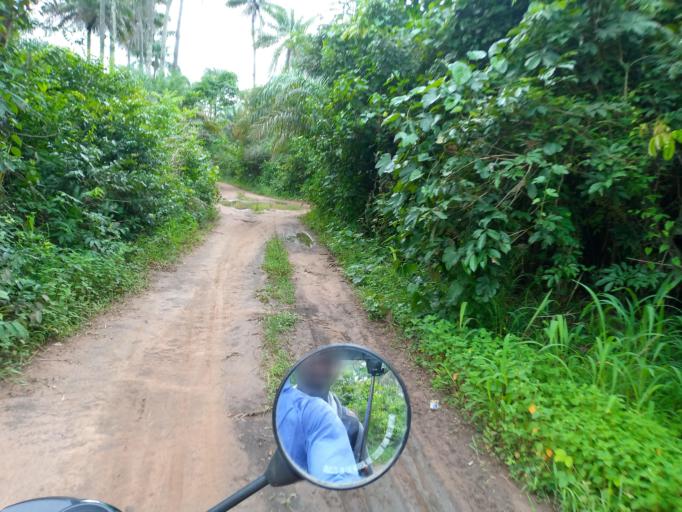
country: SL
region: Northern Province
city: Mange
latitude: 8.9805
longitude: -12.8192
